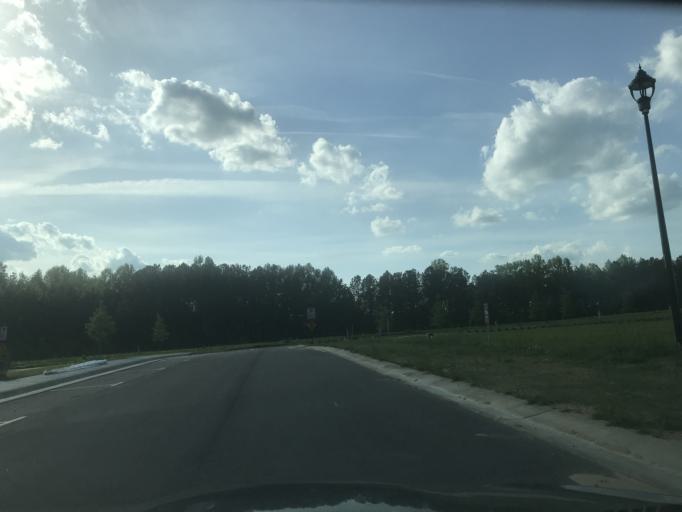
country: US
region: North Carolina
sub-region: Wake County
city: Knightdale
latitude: 35.7657
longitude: -78.4306
